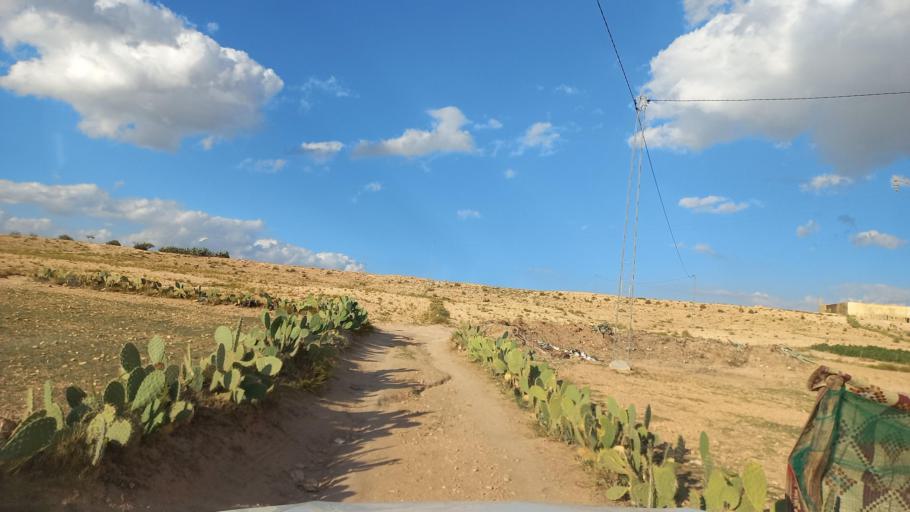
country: TN
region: Al Qasrayn
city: Sbiba
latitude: 35.3870
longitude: 9.0578
